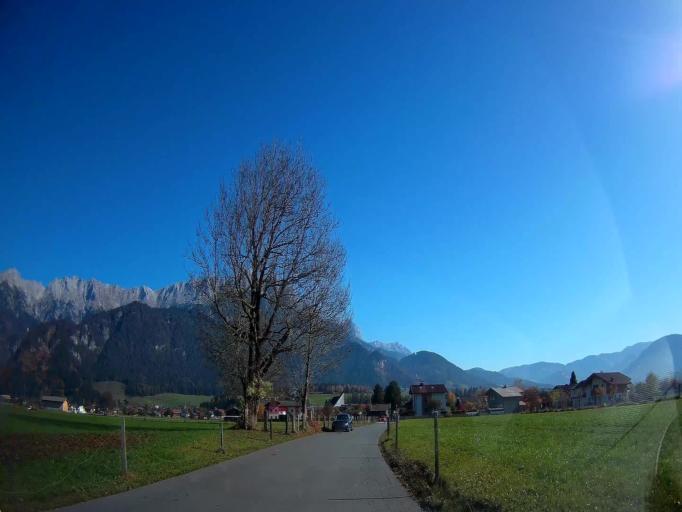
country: AT
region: Salzburg
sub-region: Politischer Bezirk Zell am See
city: Saalfelden am Steinernen Meer
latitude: 47.4479
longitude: 12.8119
